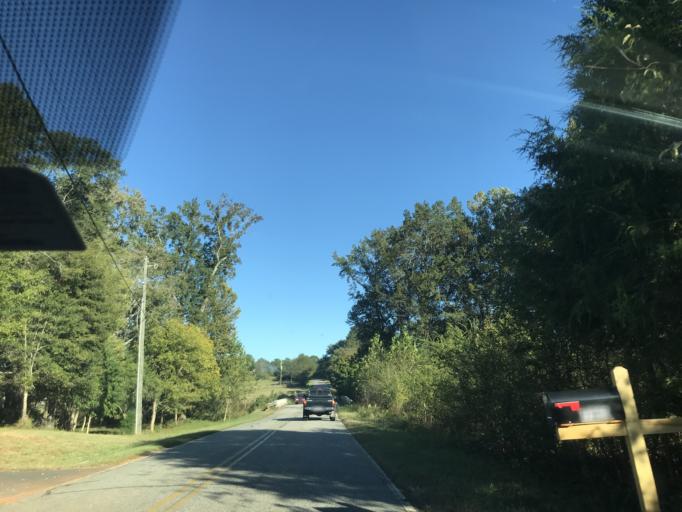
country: US
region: South Carolina
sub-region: Spartanburg County
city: Mayo
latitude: 35.1062
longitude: -81.8413
